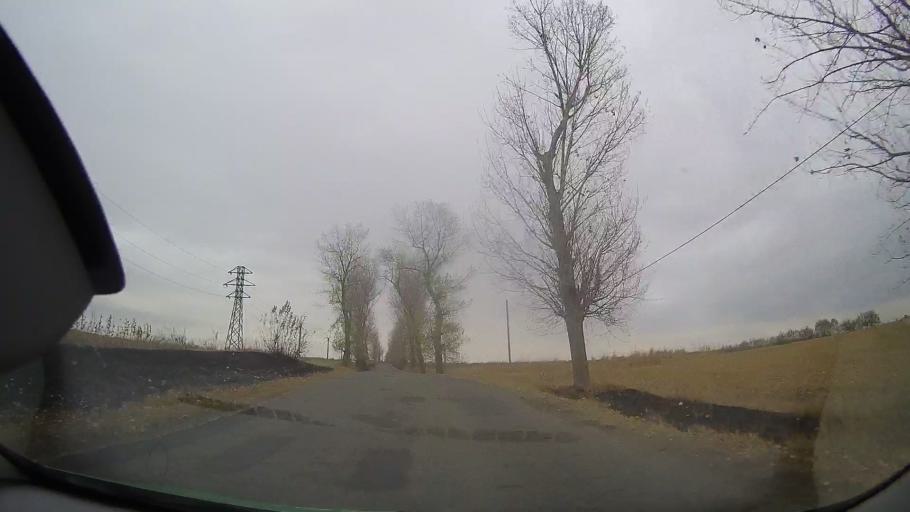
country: RO
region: Buzau
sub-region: Comuna Rusetu
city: Rusetu
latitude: 44.9486
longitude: 27.2295
